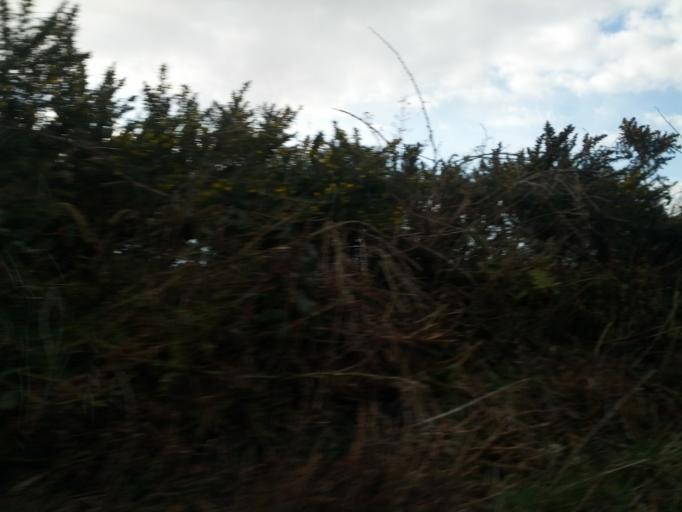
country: IE
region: Connaught
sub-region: County Galway
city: Athenry
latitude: 53.4605
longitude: -8.6461
